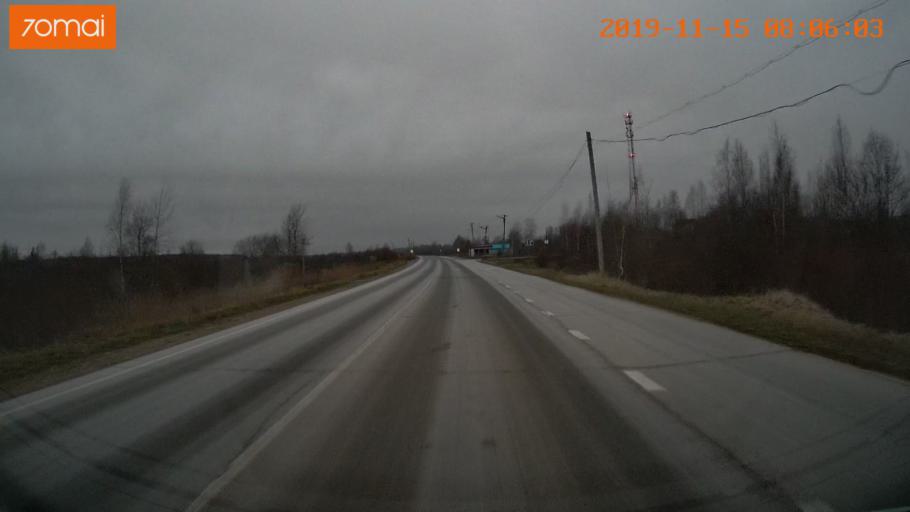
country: RU
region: Vologda
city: Cherepovets
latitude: 59.0203
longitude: 38.0459
